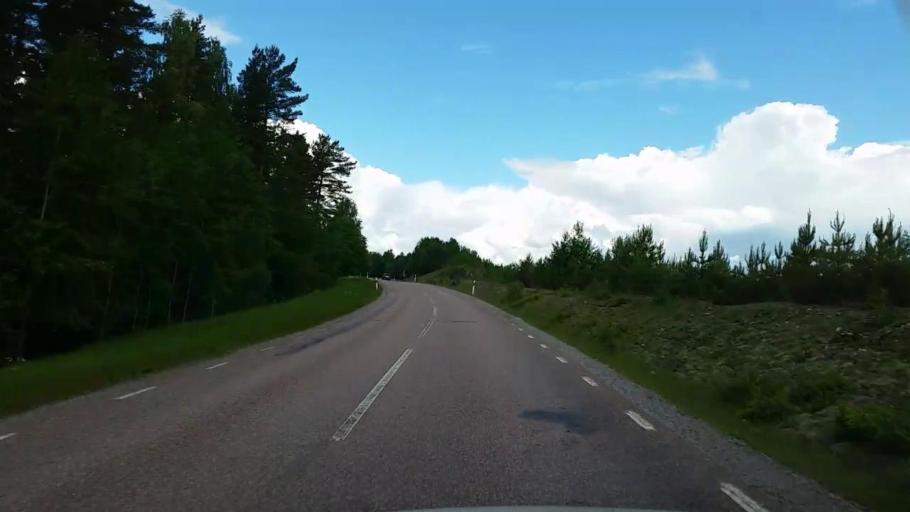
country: SE
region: Vaestmanland
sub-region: Fagersta Kommun
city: Fagersta
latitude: 59.9477
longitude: 15.7963
